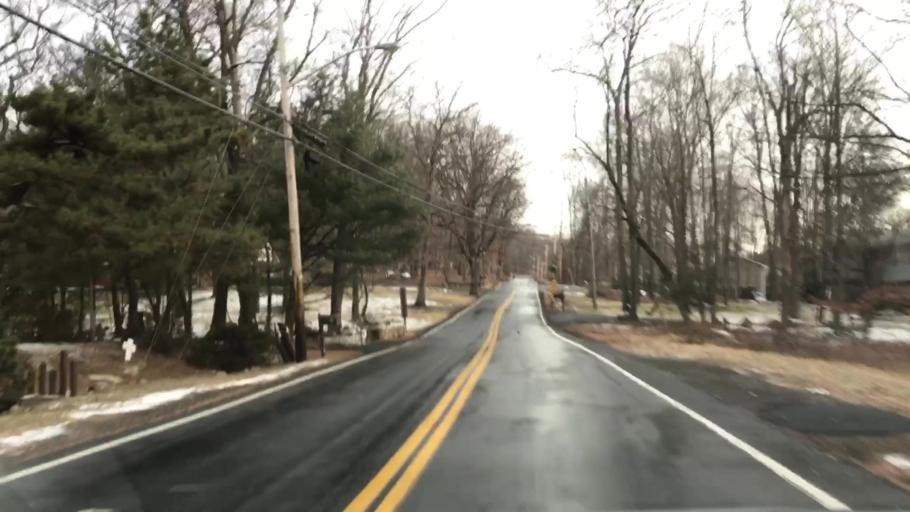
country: US
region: New York
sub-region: Rockland County
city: Thiells
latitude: 41.2282
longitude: -74.0459
